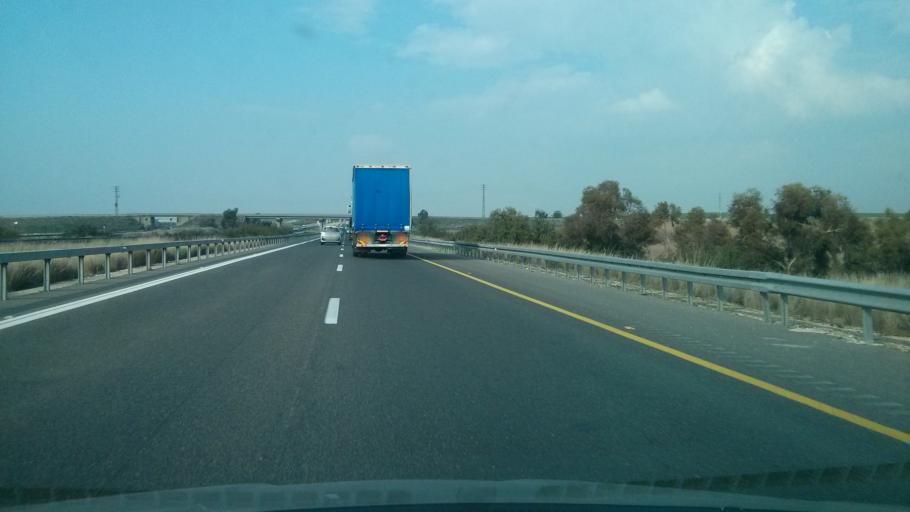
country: IL
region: Central District
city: Bene 'Ayish
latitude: 31.7416
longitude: 34.8228
